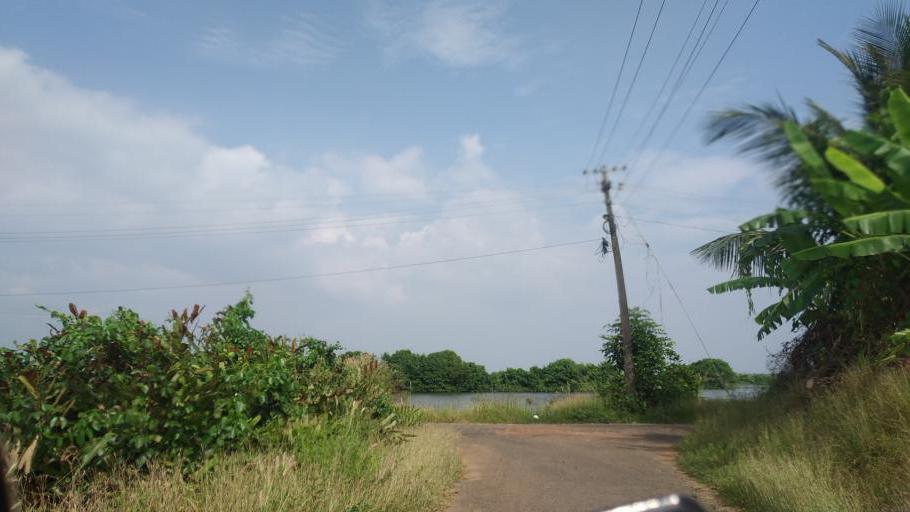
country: IN
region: Kerala
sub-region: Ernakulam
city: Elur
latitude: 10.0861
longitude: 76.2161
